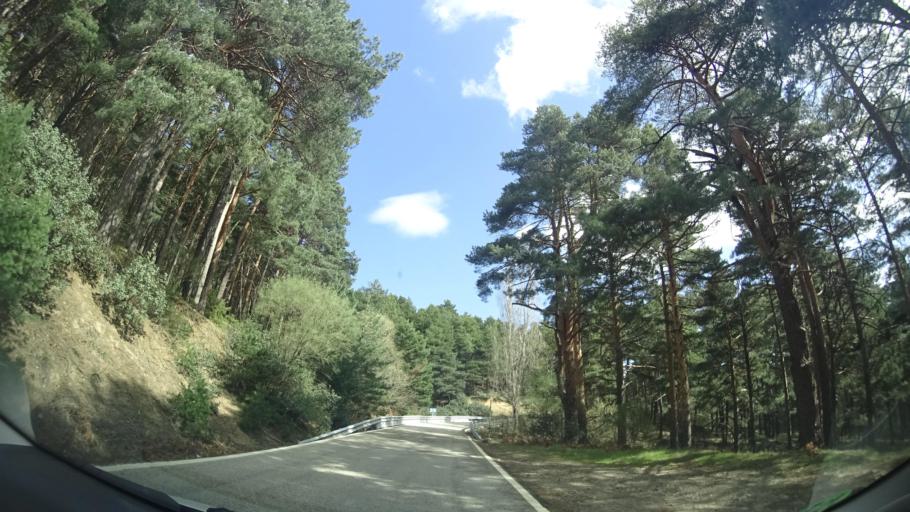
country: ES
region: Madrid
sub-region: Provincia de Madrid
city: Miraflores de la Sierra
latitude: 40.8539
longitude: -3.7670
